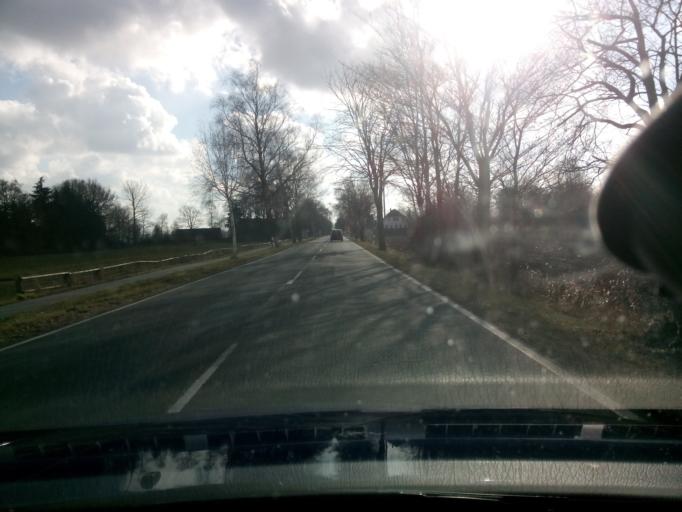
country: DE
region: Lower Saxony
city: Vollersode
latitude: 53.3166
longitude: 8.9770
